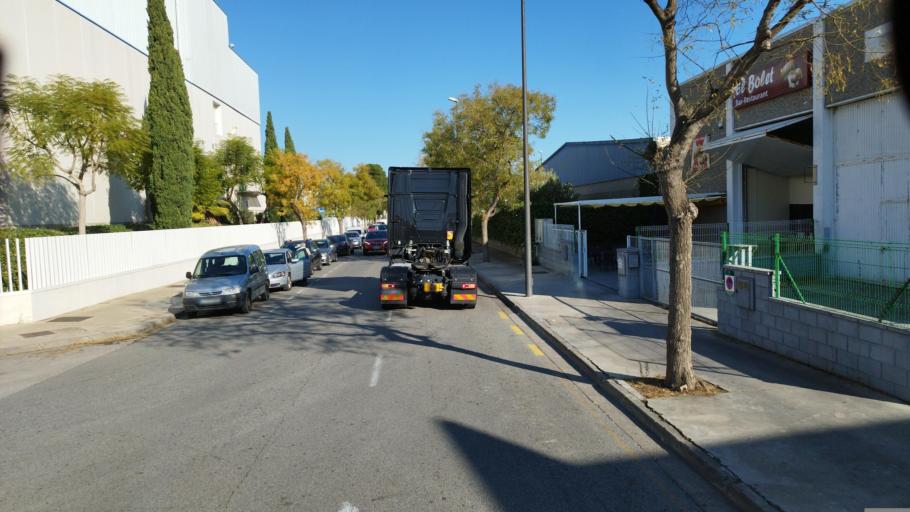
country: ES
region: Catalonia
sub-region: Provincia de Tarragona
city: Reus
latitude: 41.1569
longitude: 1.0776
